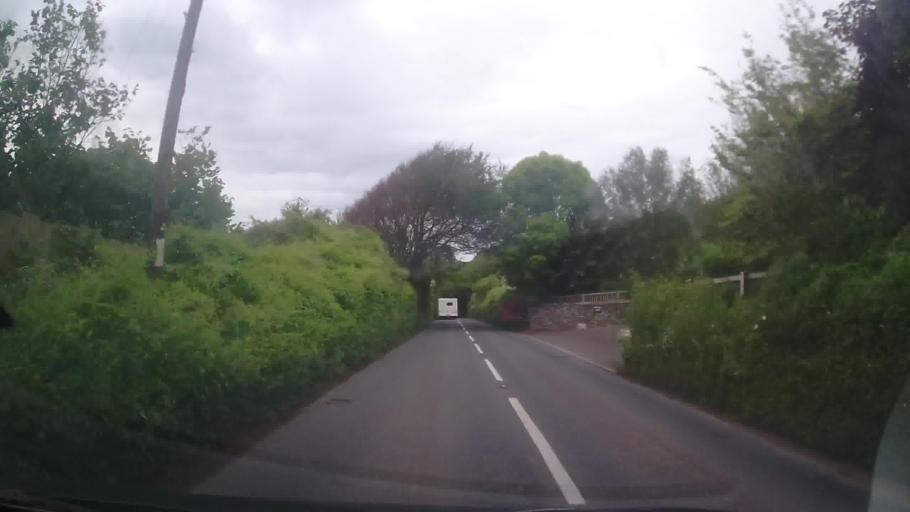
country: GB
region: England
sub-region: Devon
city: Kingsbridge
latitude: 50.2701
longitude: -3.7589
